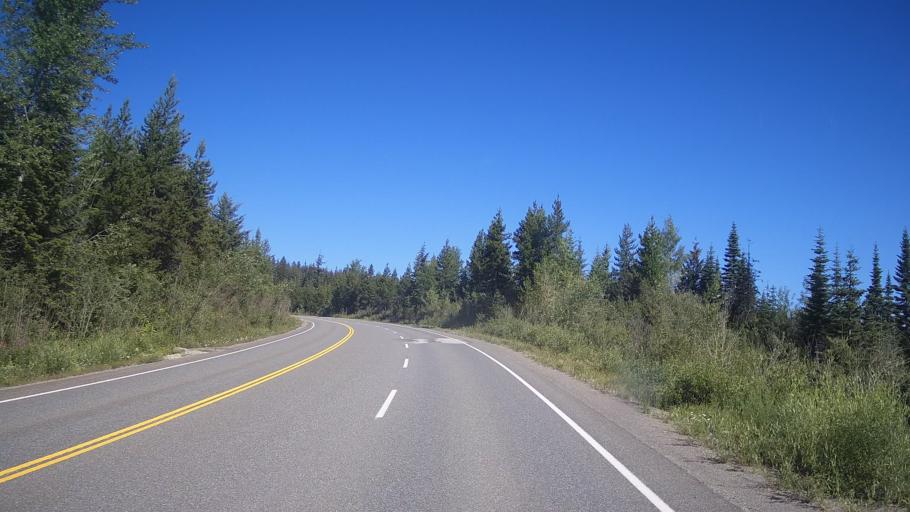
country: CA
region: British Columbia
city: Kamloops
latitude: 51.4919
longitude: -120.3252
